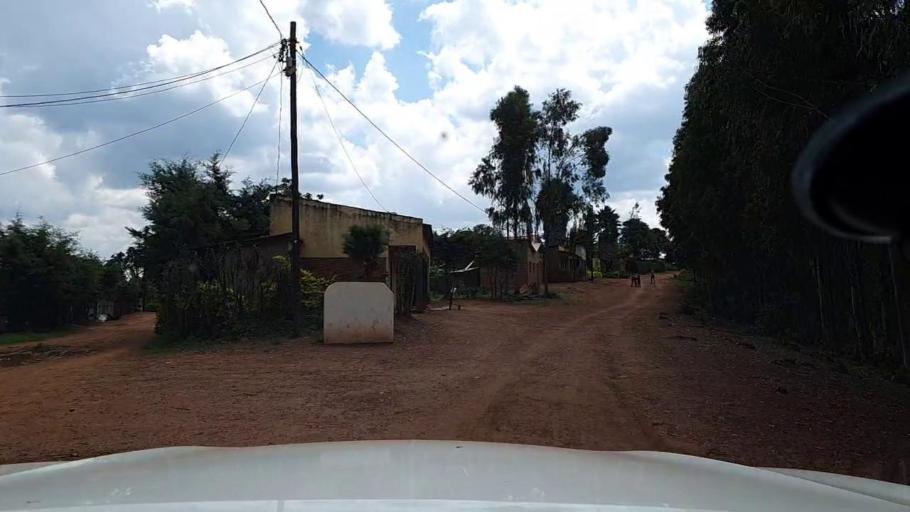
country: RW
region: Southern Province
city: Gitarama
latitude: -1.8367
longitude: 29.8331
